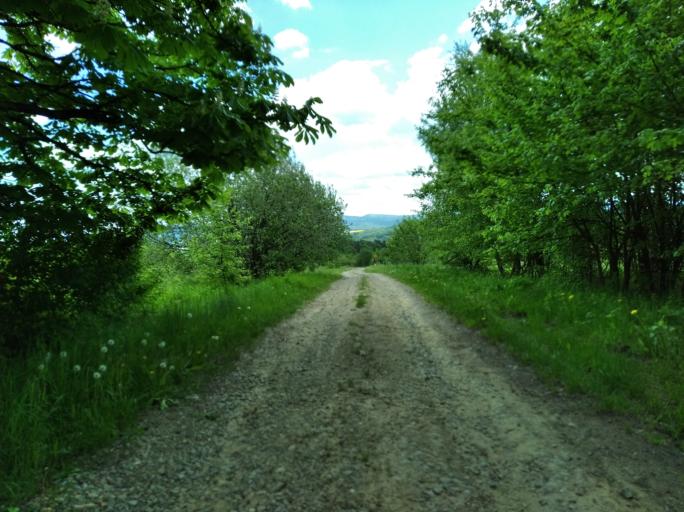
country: PL
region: Subcarpathian Voivodeship
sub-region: Powiat strzyzowski
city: Frysztak
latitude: 49.8327
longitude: 21.5478
